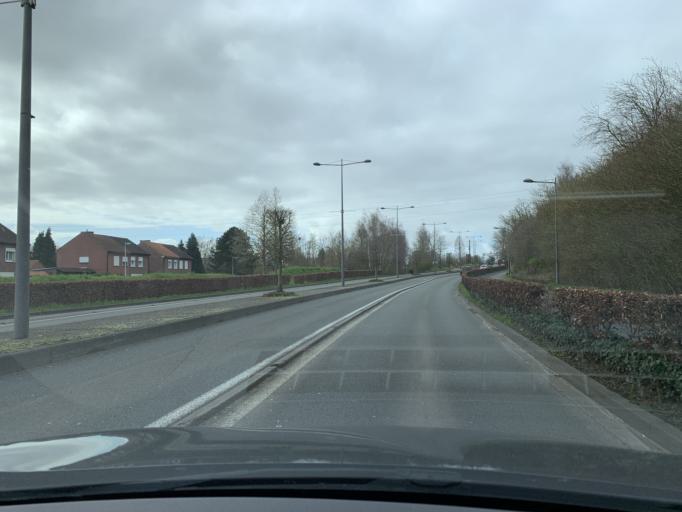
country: FR
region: Nord-Pas-de-Calais
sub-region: Departement du Nord
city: Waziers
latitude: 50.3825
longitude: 3.0960
